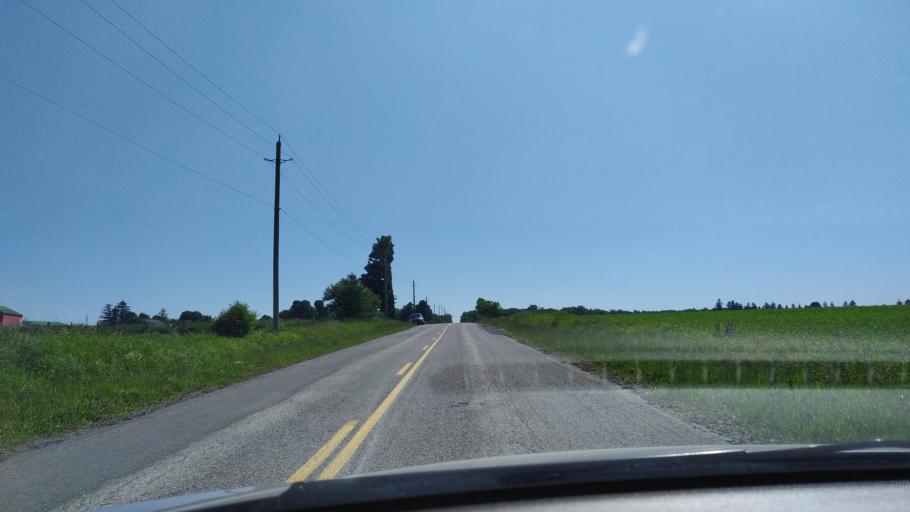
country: CA
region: Ontario
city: Waterloo
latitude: 43.4565
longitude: -80.7342
